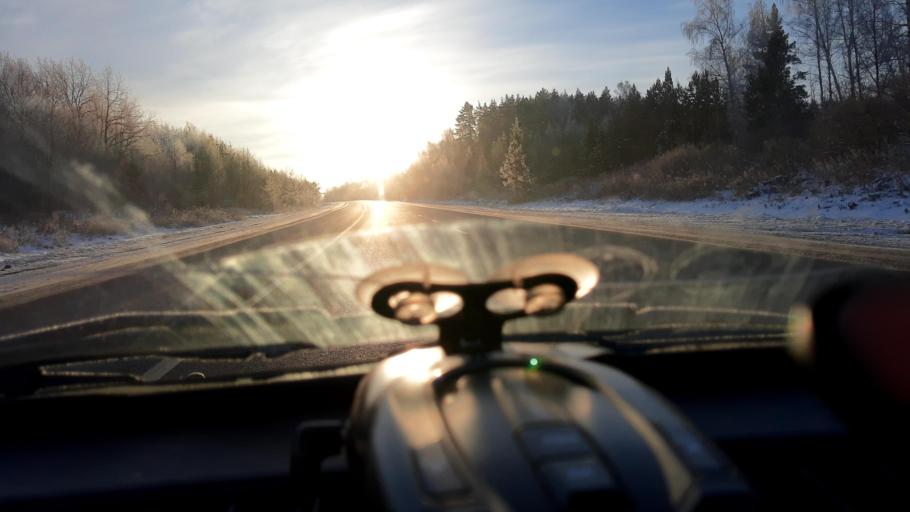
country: RU
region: Bashkortostan
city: Avdon
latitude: 54.8477
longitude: 55.7068
